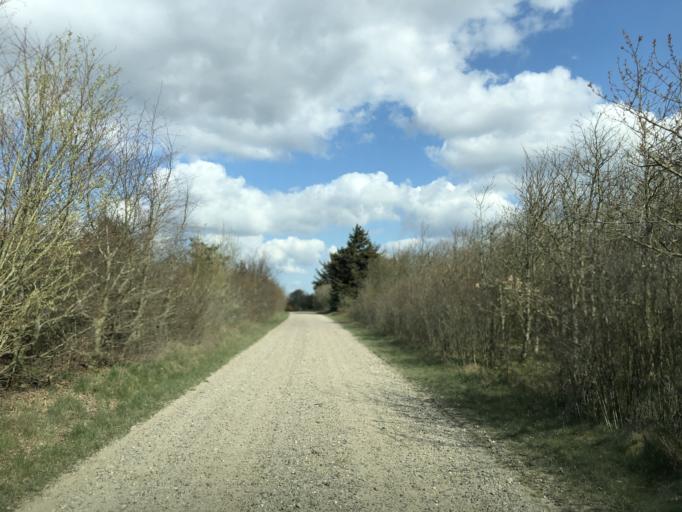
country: DK
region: Central Jutland
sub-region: Holstebro Kommune
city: Ulfborg
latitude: 56.3791
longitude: 8.2096
